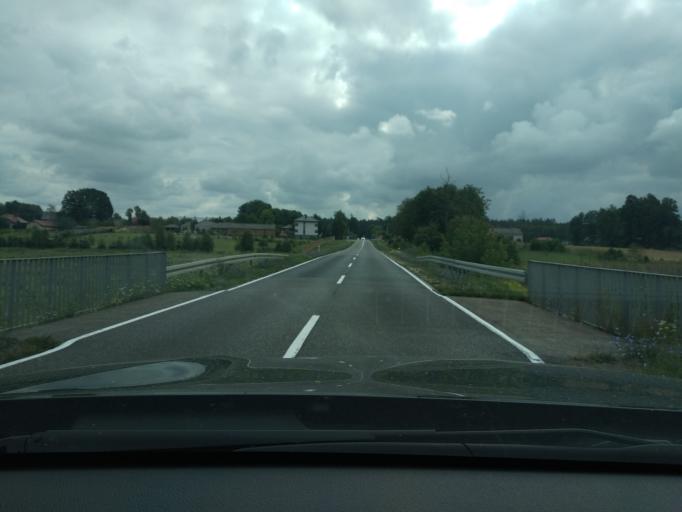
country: PL
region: Masovian Voivodeship
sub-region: Powiat pultuski
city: Obryte
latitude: 52.6487
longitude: 21.2480
